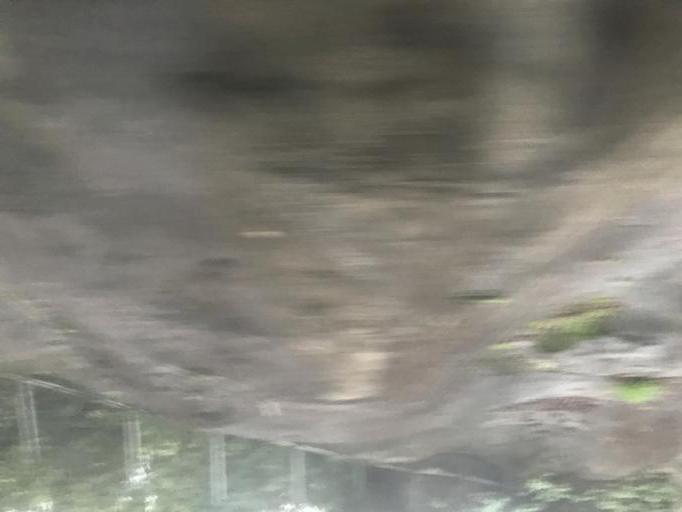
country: HK
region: Sha Tin
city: Sha Tin
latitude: 22.4124
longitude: 114.2100
